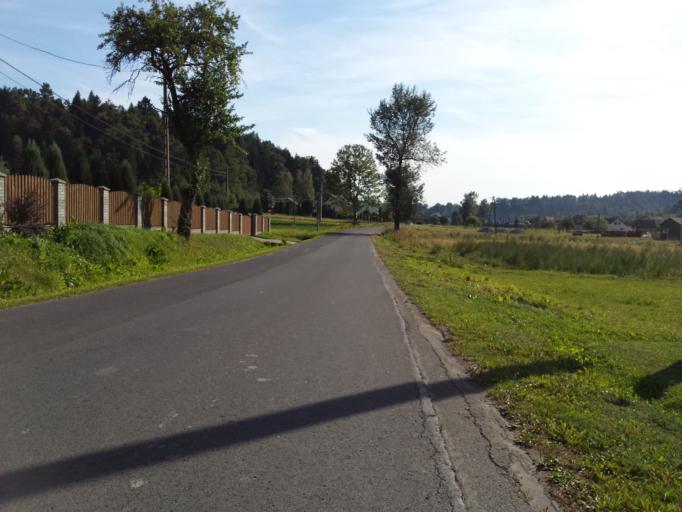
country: PL
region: Subcarpathian Voivodeship
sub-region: Powiat leski
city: Olszanica
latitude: 49.4921
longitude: 22.4488
